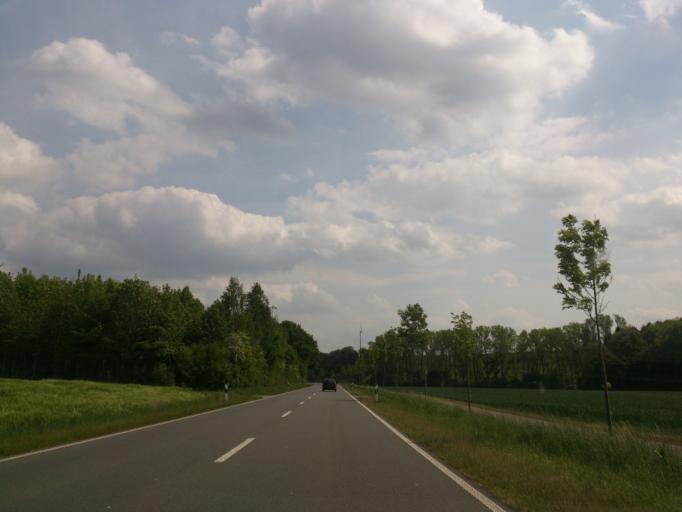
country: DE
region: North Rhine-Westphalia
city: Bad Lippspringe
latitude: 51.7519
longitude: 8.8347
